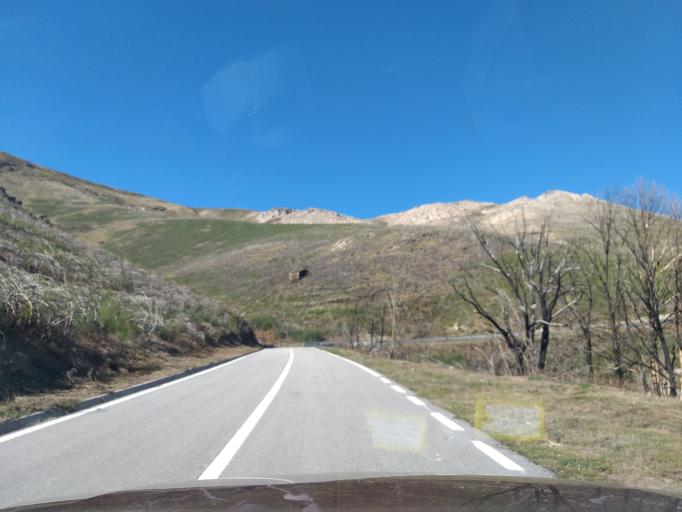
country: PT
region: Guarda
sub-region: Manteigas
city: Manteigas
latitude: 40.4696
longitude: -7.5203
